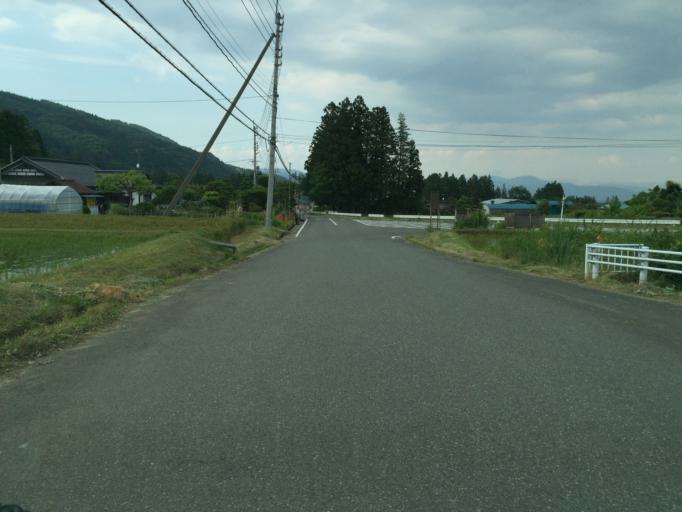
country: JP
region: Fukushima
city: Fukushima-shi
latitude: 37.7116
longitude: 140.3514
